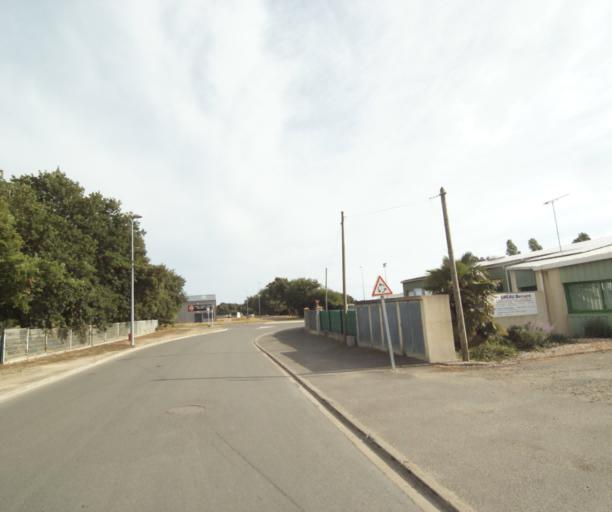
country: FR
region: Pays de la Loire
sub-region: Departement de la Vendee
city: Chateau-d'Olonne
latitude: 46.4889
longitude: -1.7283
